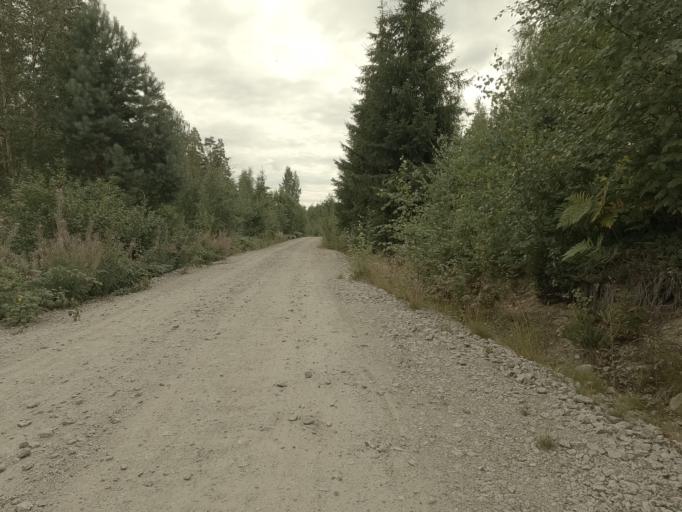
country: RU
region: Leningrad
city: Kamennogorsk
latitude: 60.9831
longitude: 29.1761
